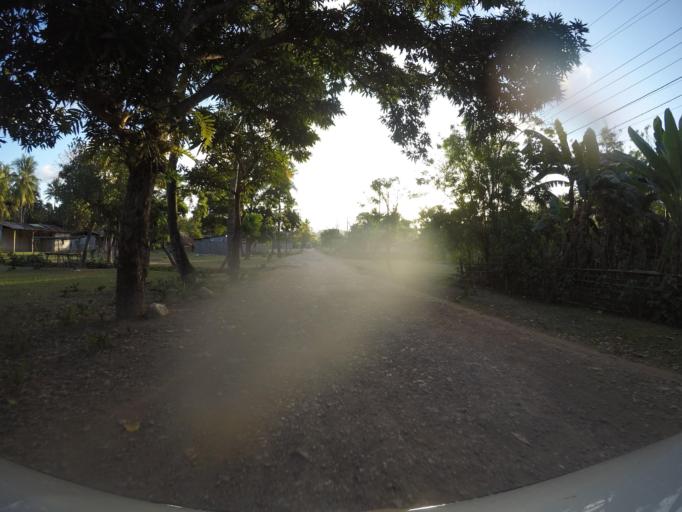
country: TL
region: Baucau
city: Venilale
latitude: -8.7474
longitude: 126.7098
